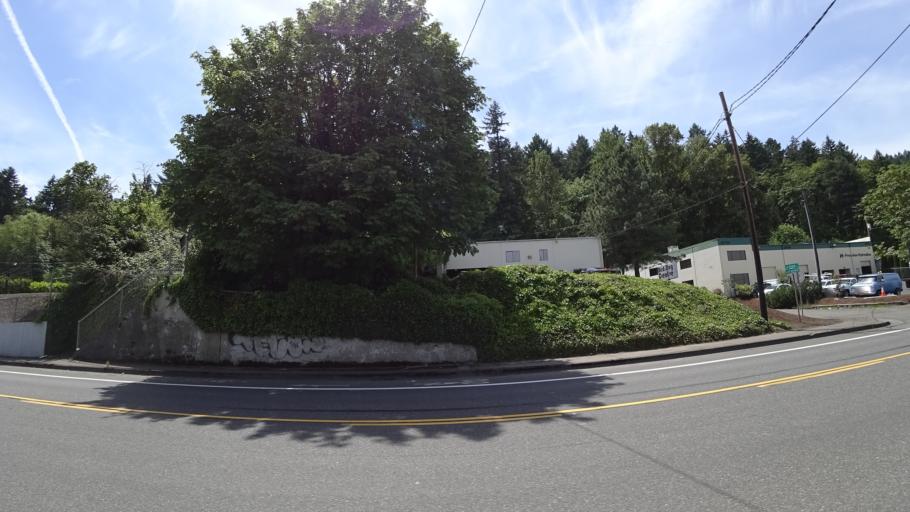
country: US
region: Oregon
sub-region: Multnomah County
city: Portland
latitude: 45.5417
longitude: -122.7195
